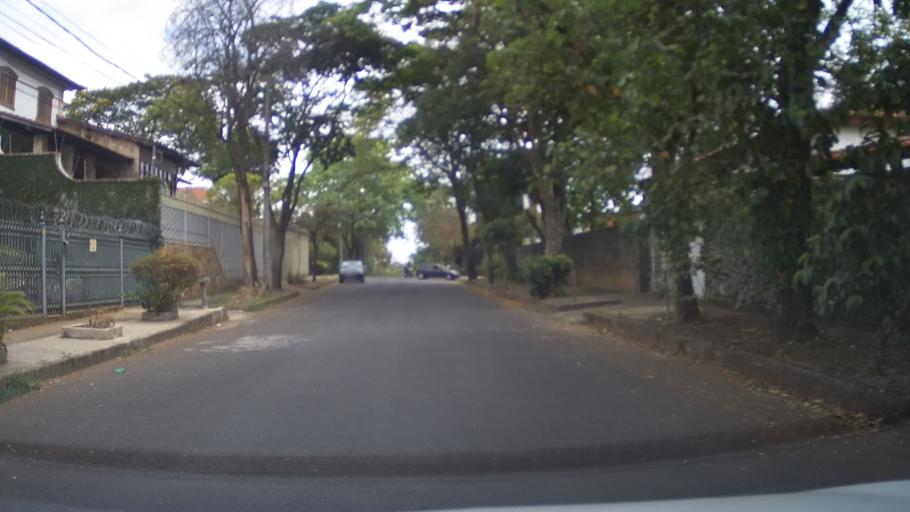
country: BR
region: Minas Gerais
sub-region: Belo Horizonte
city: Belo Horizonte
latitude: -19.8542
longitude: -43.9640
